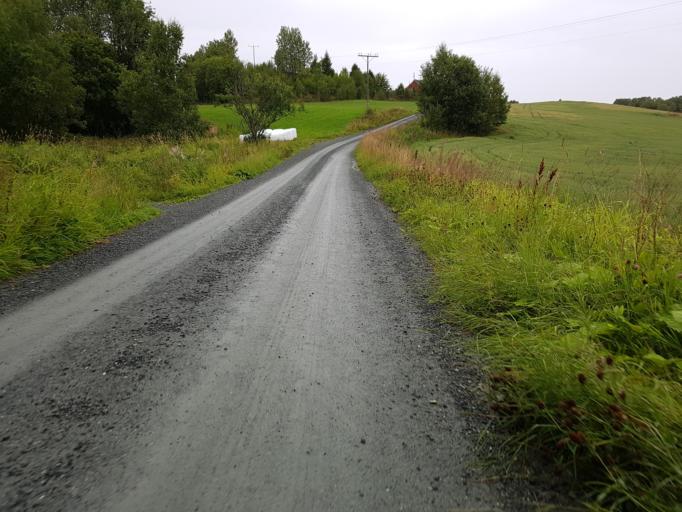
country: NO
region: Sor-Trondelag
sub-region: Trondheim
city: Trondheim
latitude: 63.4017
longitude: 10.4612
